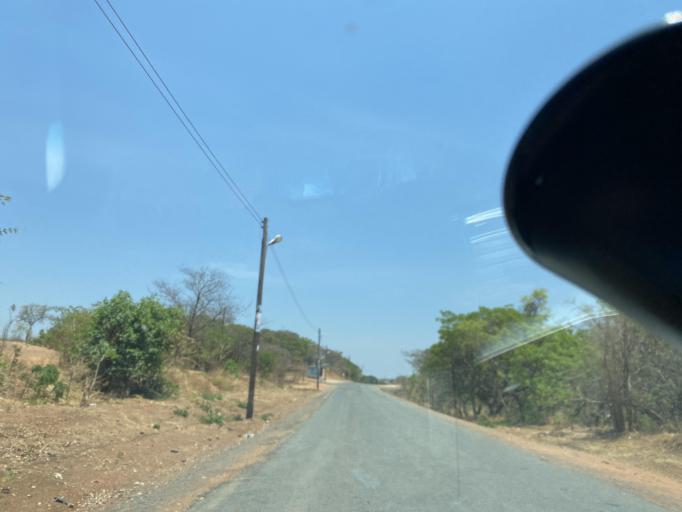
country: ZM
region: Lusaka
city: Kafue
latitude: -15.8667
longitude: 28.4398
